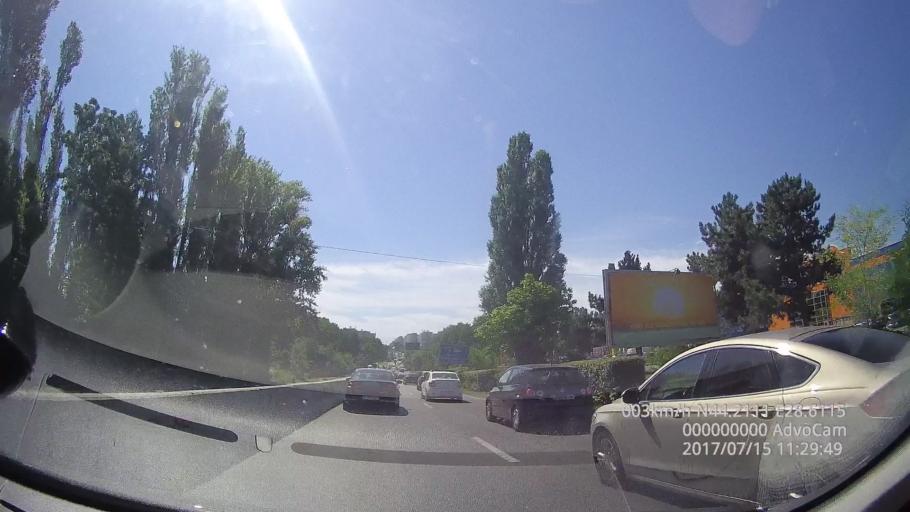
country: RO
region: Constanta
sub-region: Municipiul Constanta
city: Palazu Mare
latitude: 44.2110
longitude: 28.6116
